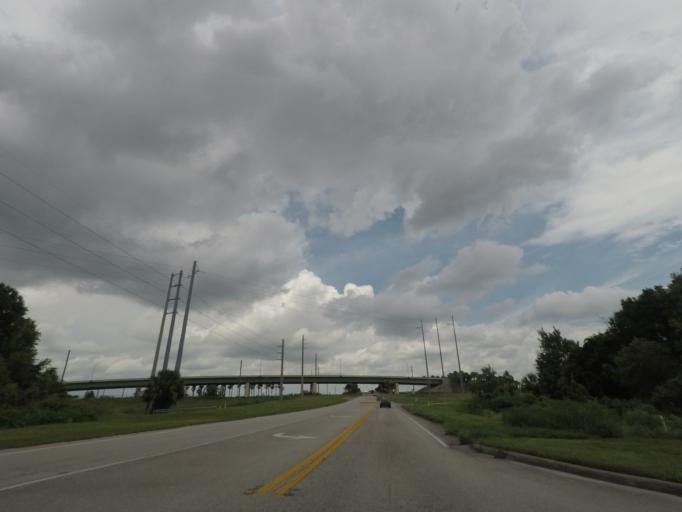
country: US
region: Florida
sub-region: Polk County
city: Loughman
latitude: 28.2810
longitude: -81.5905
